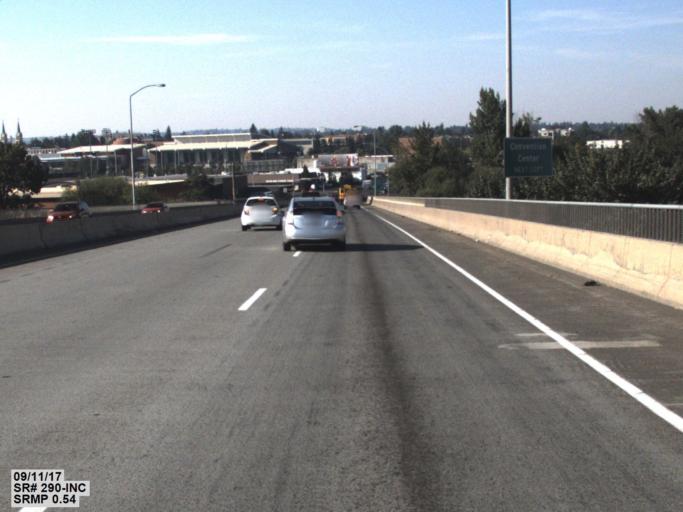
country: US
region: Washington
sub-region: Spokane County
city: Spokane
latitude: 47.6590
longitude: -117.3955
